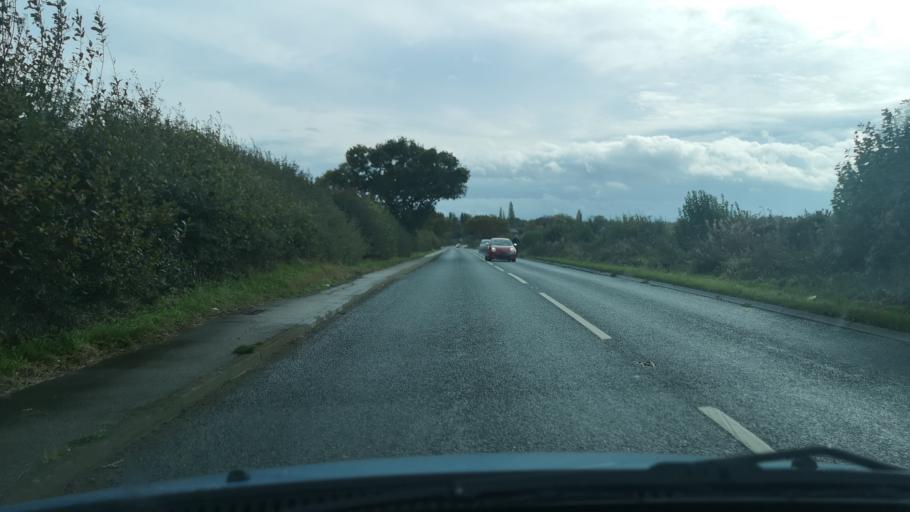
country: GB
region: England
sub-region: City and Borough of Wakefield
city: Fitzwilliam
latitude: 53.6423
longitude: -1.3855
